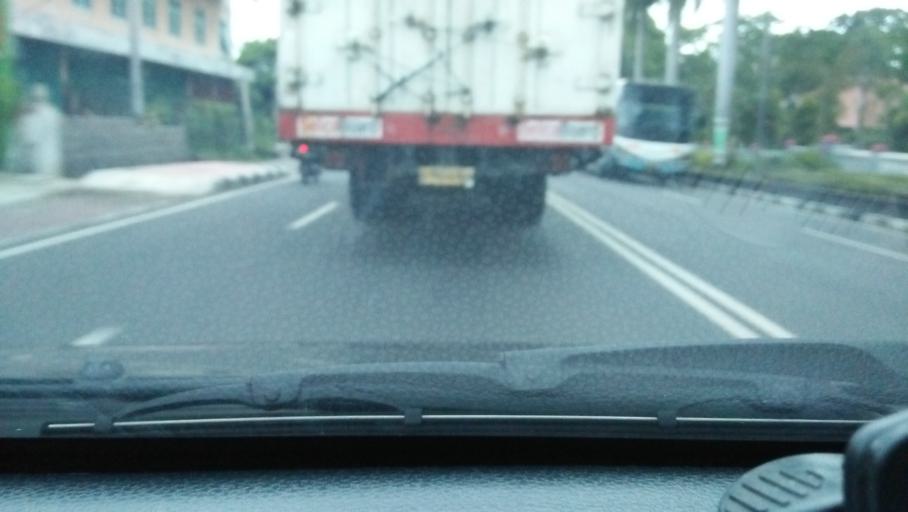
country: ID
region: Central Java
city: Magelang
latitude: -7.4400
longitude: 110.2268
